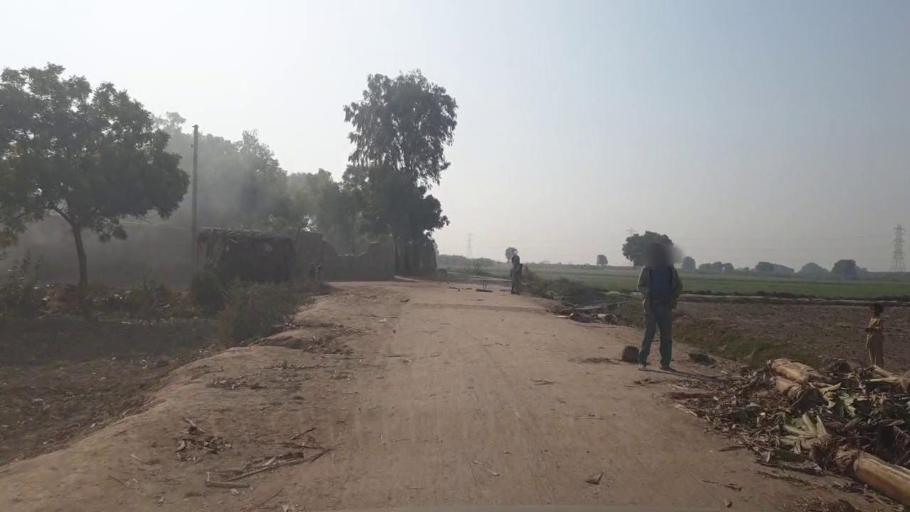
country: PK
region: Sindh
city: Tando Allahyar
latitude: 25.4638
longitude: 68.7634
